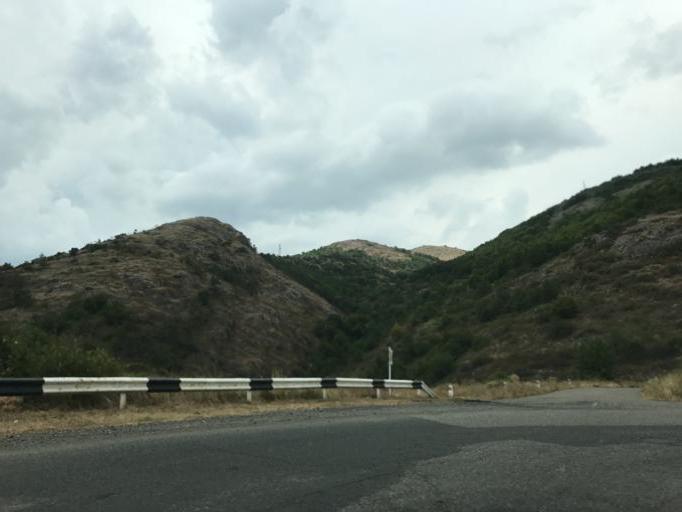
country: AZ
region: Lacin
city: Lacin
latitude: 39.6769
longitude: 46.6282
